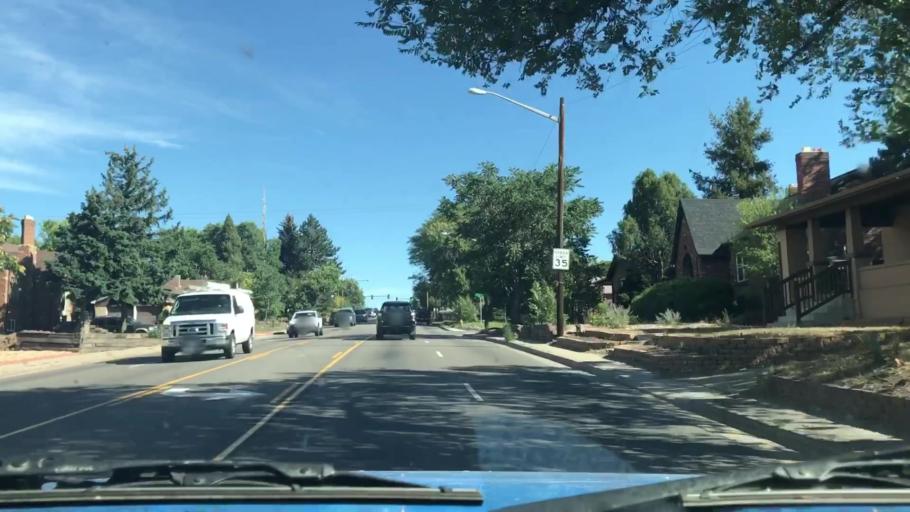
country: US
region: Colorado
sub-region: Jefferson County
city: Edgewater
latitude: 39.7593
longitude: -105.0532
